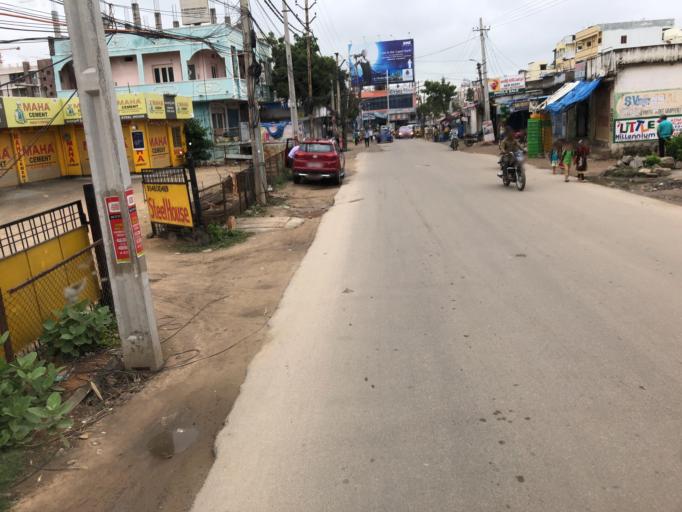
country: IN
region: Telangana
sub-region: Medak
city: Serilingampalle
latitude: 17.4655
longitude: 78.3428
